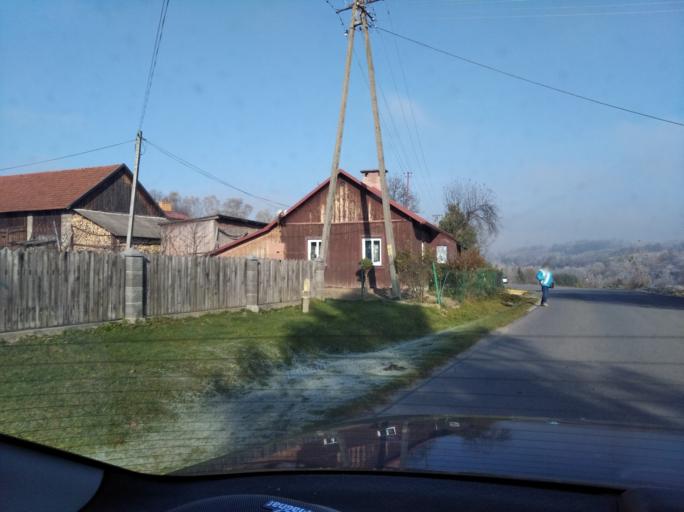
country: PL
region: Subcarpathian Voivodeship
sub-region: Powiat strzyzowski
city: Wysoka Strzyzowska
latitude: 49.8337
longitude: 21.7409
